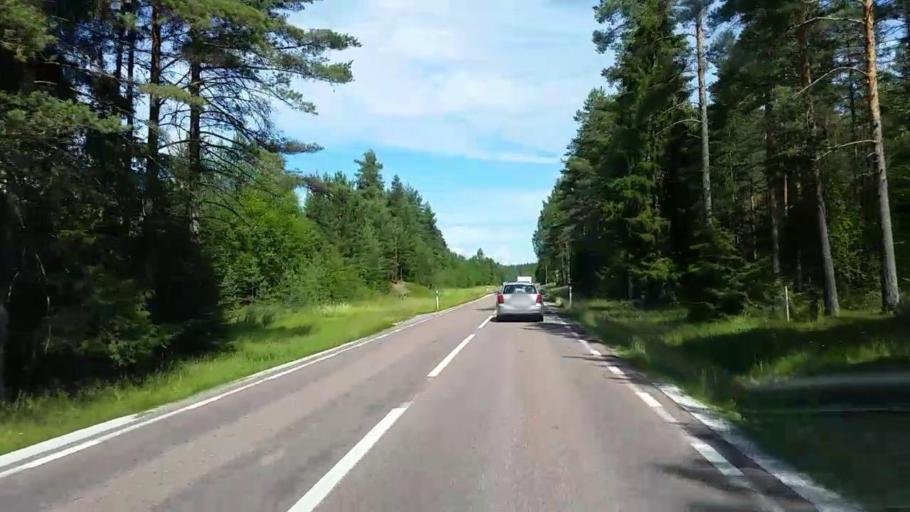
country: SE
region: Dalarna
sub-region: Rattviks Kommun
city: Raettvik
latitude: 60.9169
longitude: 15.2042
